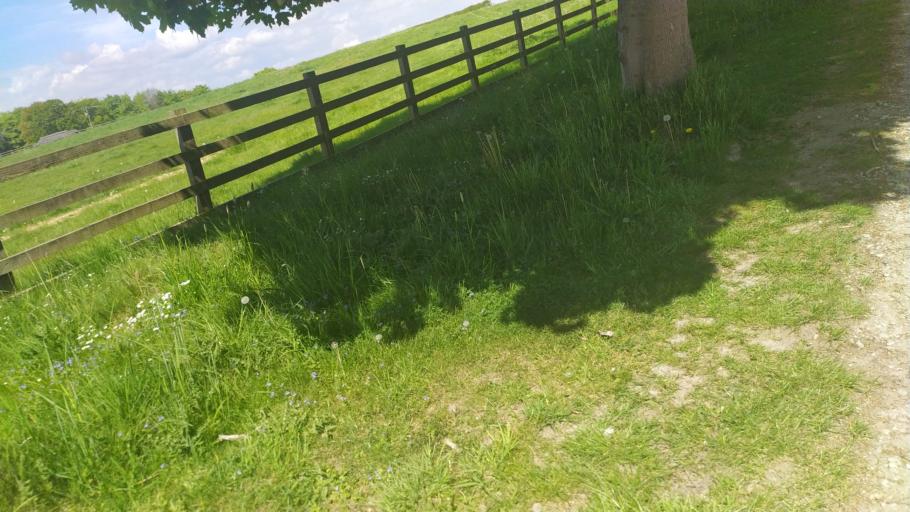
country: GB
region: England
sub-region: City and Borough of Leeds
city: Chapel Allerton
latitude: 53.8937
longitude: -1.5351
